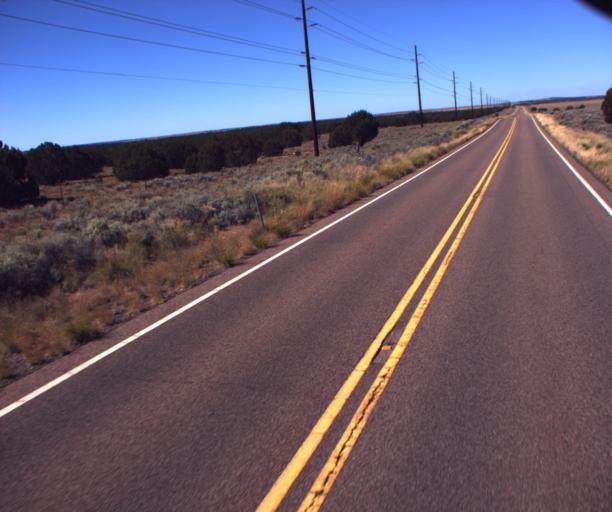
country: US
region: Arizona
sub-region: Navajo County
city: Taylor
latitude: 34.4834
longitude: -110.2674
